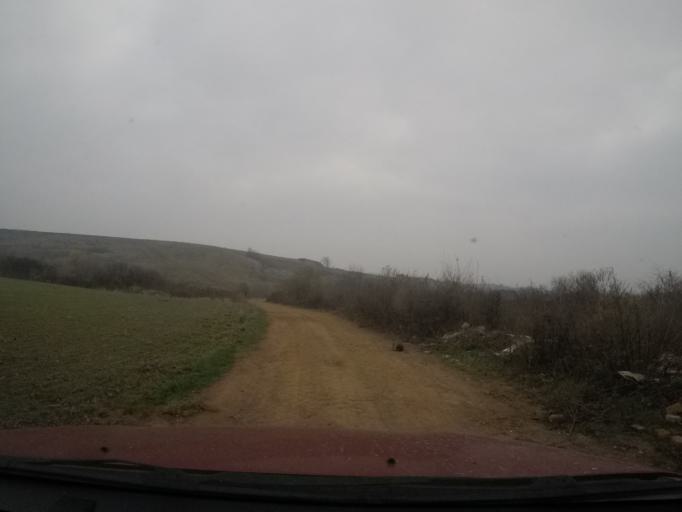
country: SK
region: Presovsky
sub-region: Okres Presov
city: Presov
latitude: 48.8837
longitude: 21.2763
